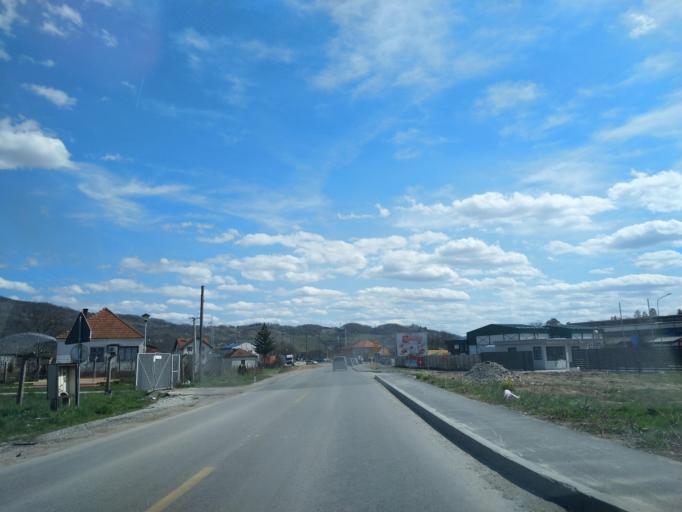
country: RS
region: Central Serbia
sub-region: Zlatiborski Okrug
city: Arilje
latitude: 43.7575
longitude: 20.0993
